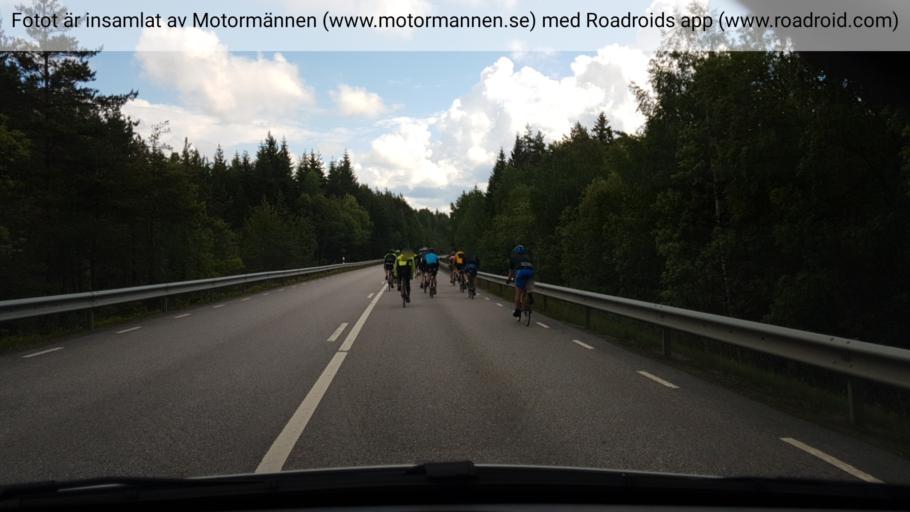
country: SE
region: Vaestra Goetaland
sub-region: Karlsborgs Kommun
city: Karlsborg
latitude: 58.6607
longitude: 14.5928
